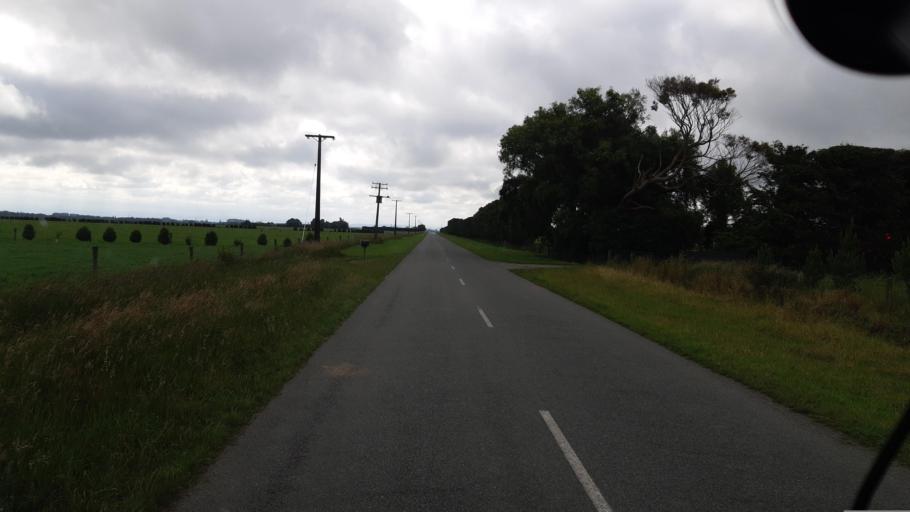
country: NZ
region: Canterbury
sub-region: Timaru District
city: Timaru
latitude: -44.2421
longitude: 171.3563
